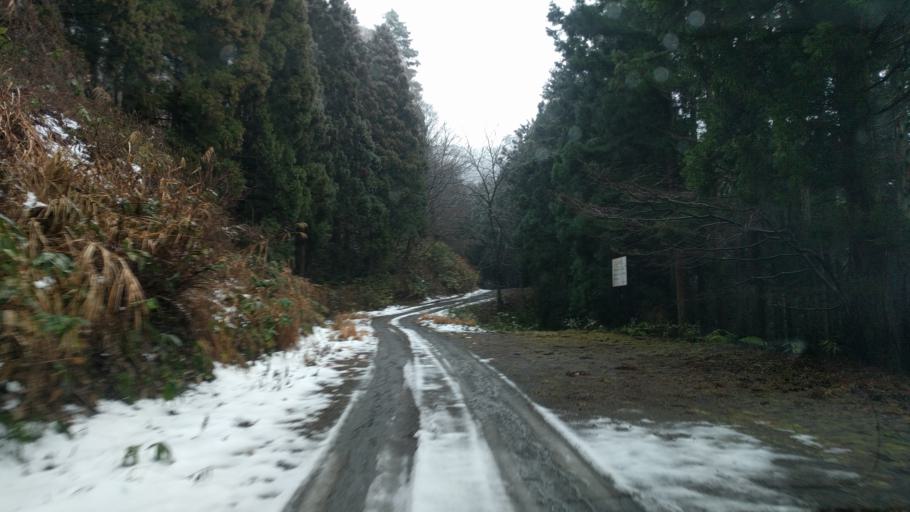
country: JP
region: Fukushima
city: Inawashiro
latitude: 37.5774
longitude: 139.9821
